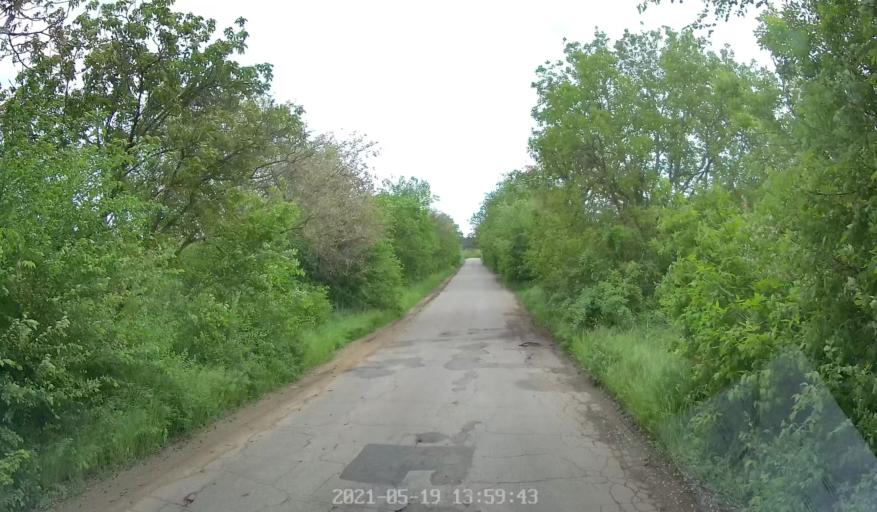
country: MD
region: Chisinau
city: Chisinau
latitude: 47.0389
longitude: 28.9259
